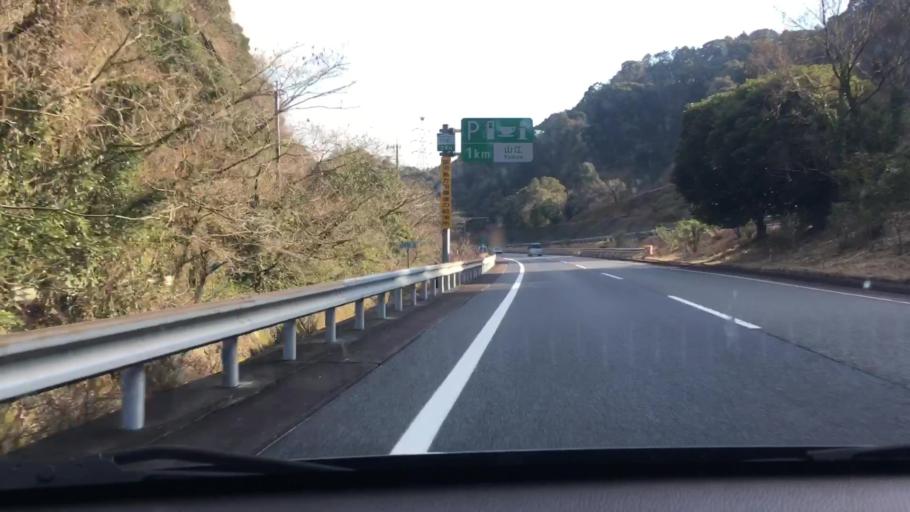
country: JP
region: Kumamoto
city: Hitoyoshi
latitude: 32.2697
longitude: 130.7606
